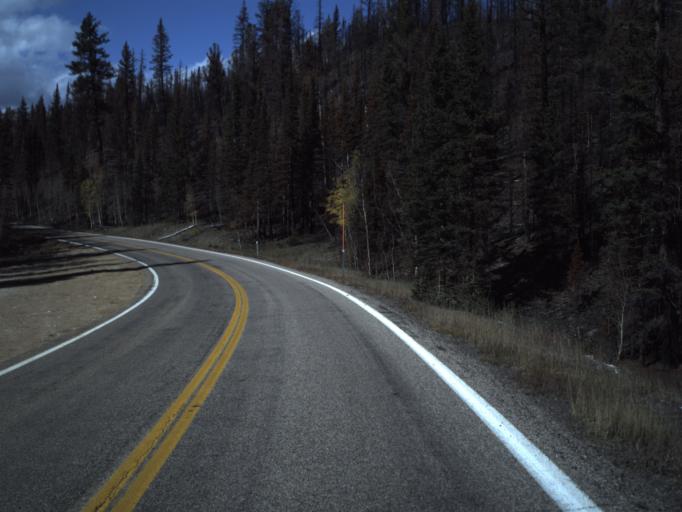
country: US
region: Utah
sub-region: Iron County
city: Parowan
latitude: 37.6582
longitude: -112.7154
